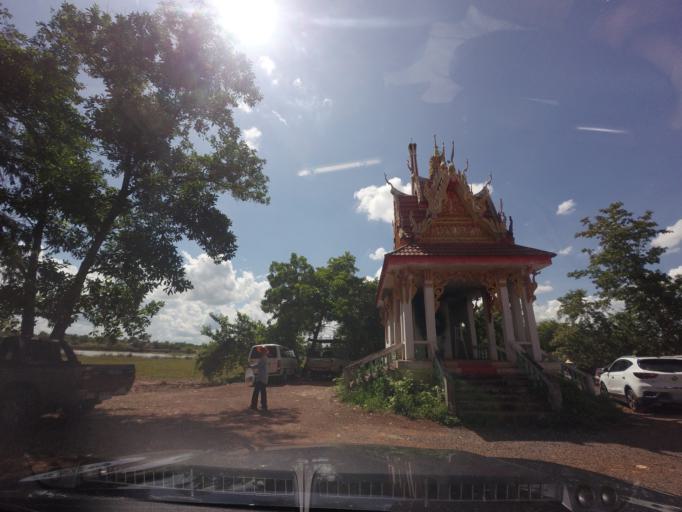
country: TH
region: Changwat Udon Thani
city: Ban Dung
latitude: 17.7444
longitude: 103.3580
